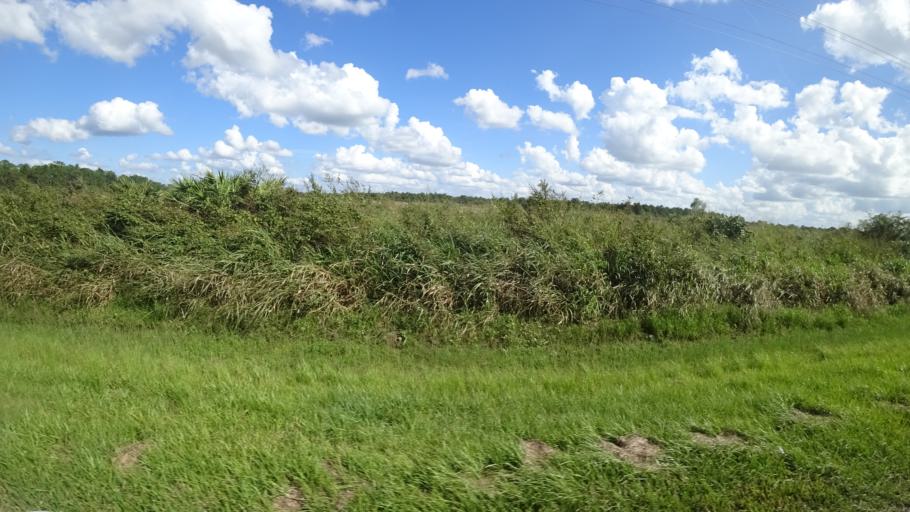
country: US
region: Florida
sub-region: Sarasota County
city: Lake Sarasota
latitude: 27.3797
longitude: -82.1398
